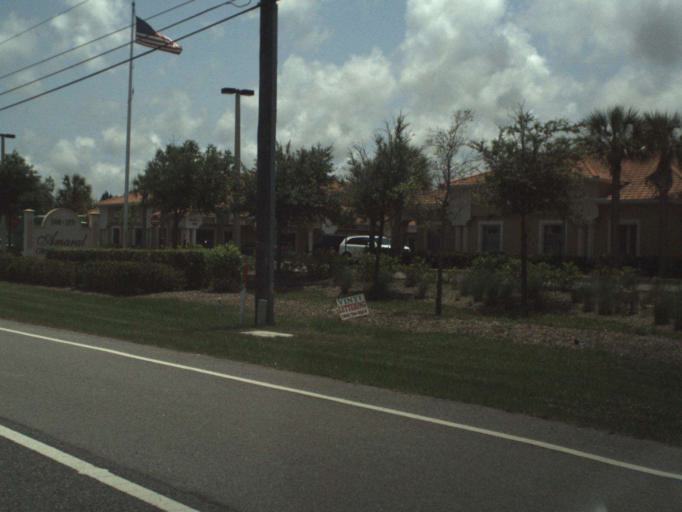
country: US
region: Florida
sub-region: Volusia County
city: Ormond-by-the-Sea
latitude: 29.3265
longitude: -81.1185
